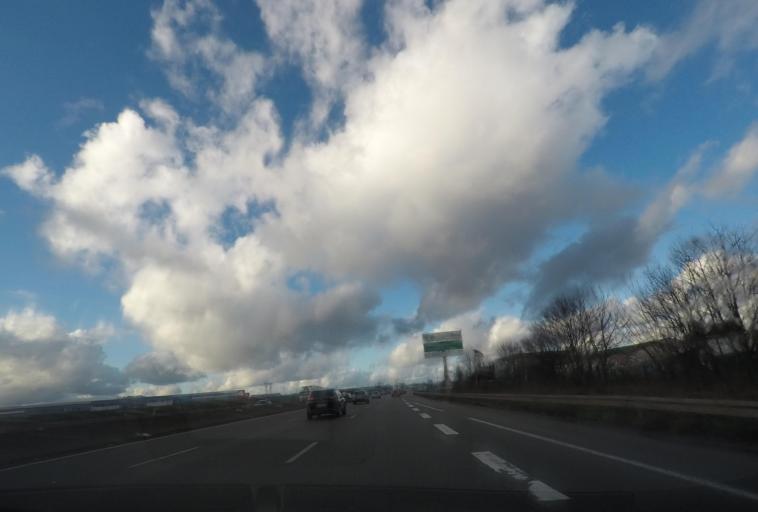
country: FR
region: Ile-de-France
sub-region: Departement de l'Essonne
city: Le Coudray-Montceaux
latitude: 48.5641
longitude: 2.4775
